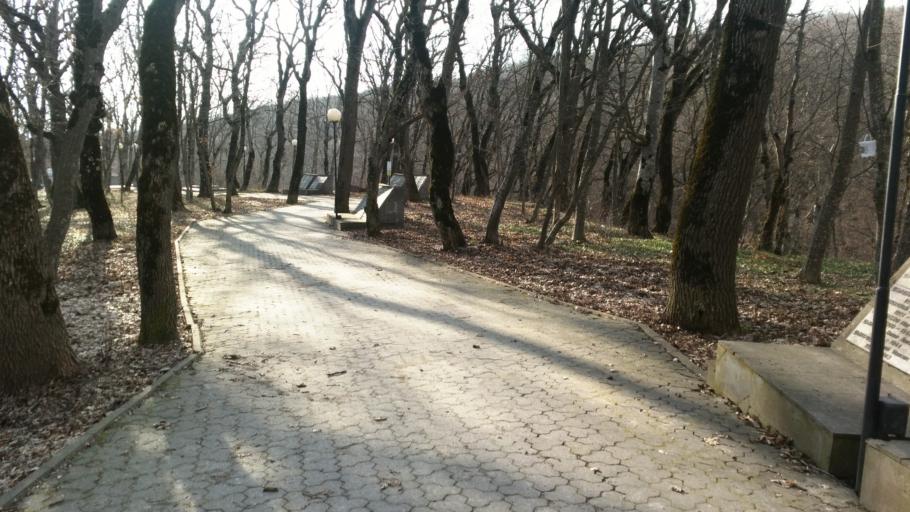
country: RU
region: Stavropol'skiy
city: Zheleznovodsk
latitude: 44.1327
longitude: 43.0408
